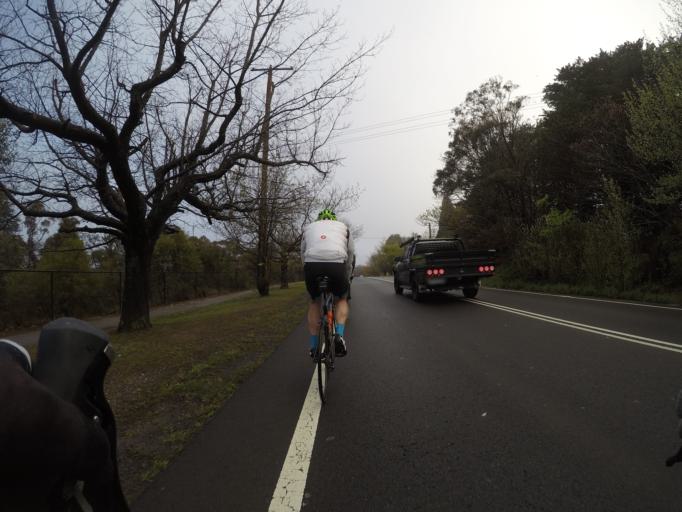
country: AU
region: New South Wales
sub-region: Blue Mountains Municipality
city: Blackheath
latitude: -33.6305
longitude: 150.2845
